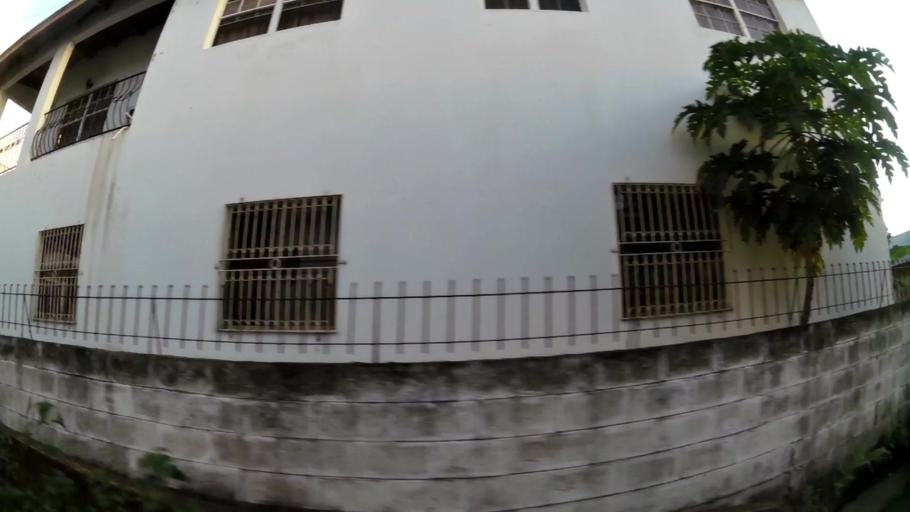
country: KN
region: Saint Anne Sandy Point
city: Sandy Point Town
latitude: 17.3620
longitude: -62.8498
